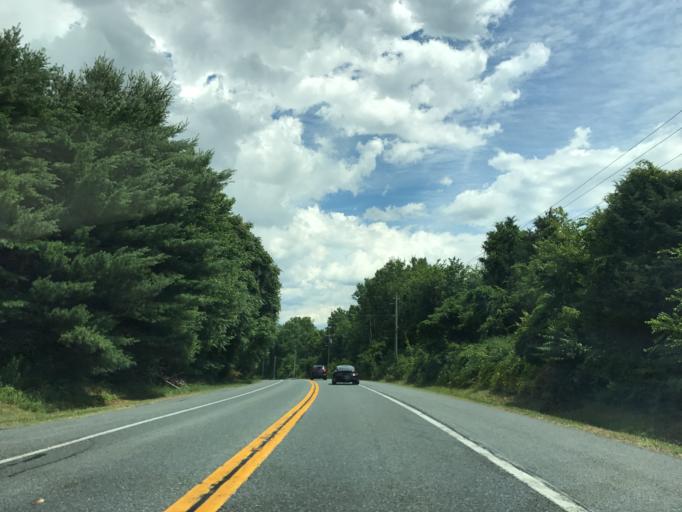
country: US
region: Maryland
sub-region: Harford County
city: Jarrettsville
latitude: 39.6560
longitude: -76.4558
